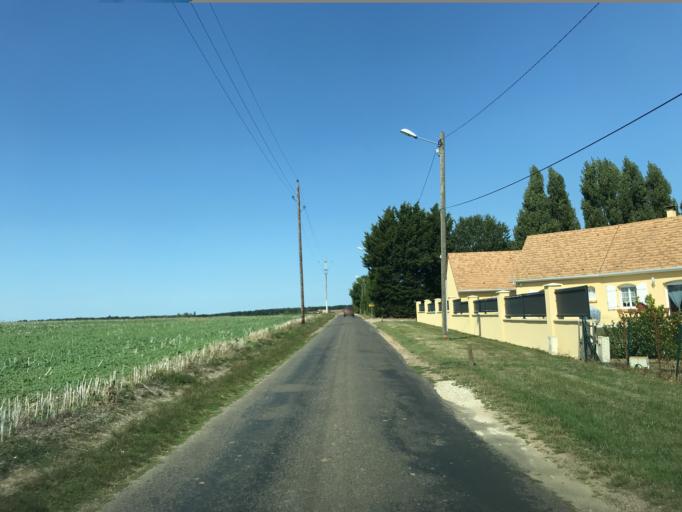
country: FR
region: Haute-Normandie
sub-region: Departement de l'Eure
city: Houlbec-Cocherel
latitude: 49.0615
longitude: 1.2700
